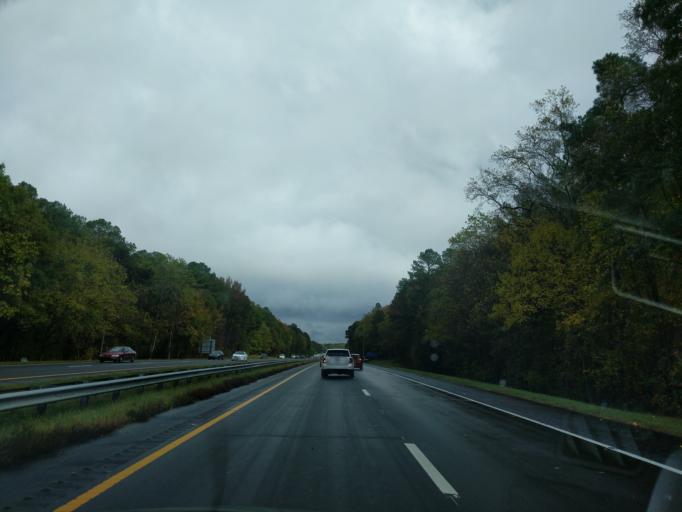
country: US
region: North Carolina
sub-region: Durham County
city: Durham
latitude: 36.0379
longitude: -78.9936
